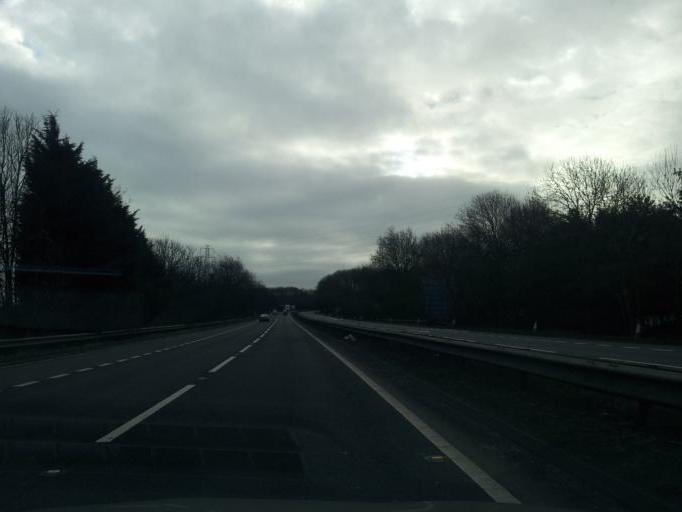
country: GB
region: England
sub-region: Lincolnshire
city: Grantham
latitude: 52.8966
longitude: -0.6606
